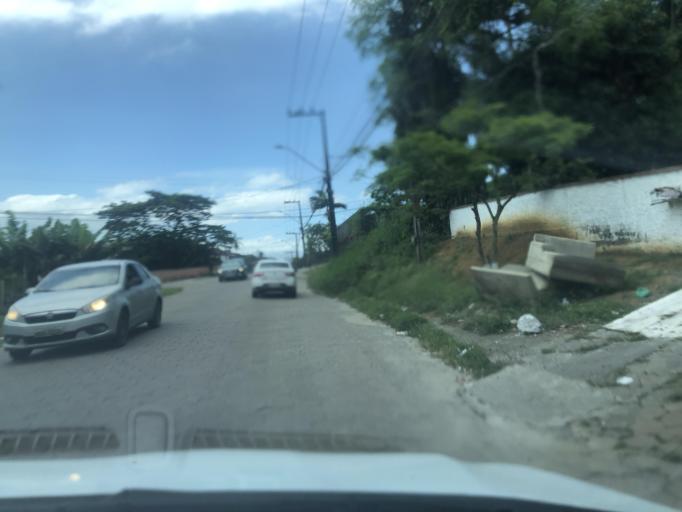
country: BR
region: Santa Catarina
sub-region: Joinville
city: Joinville
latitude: -26.3390
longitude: -48.8089
